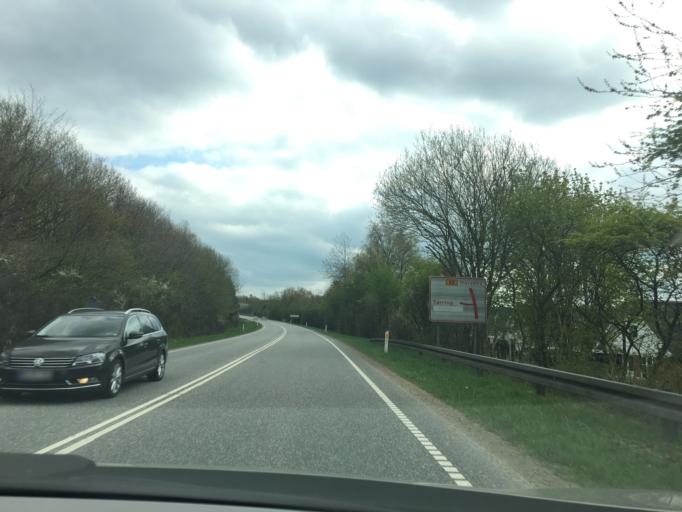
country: DK
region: Central Jutland
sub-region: Horsens Kommune
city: Braedstrup
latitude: 55.9682
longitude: 9.6027
